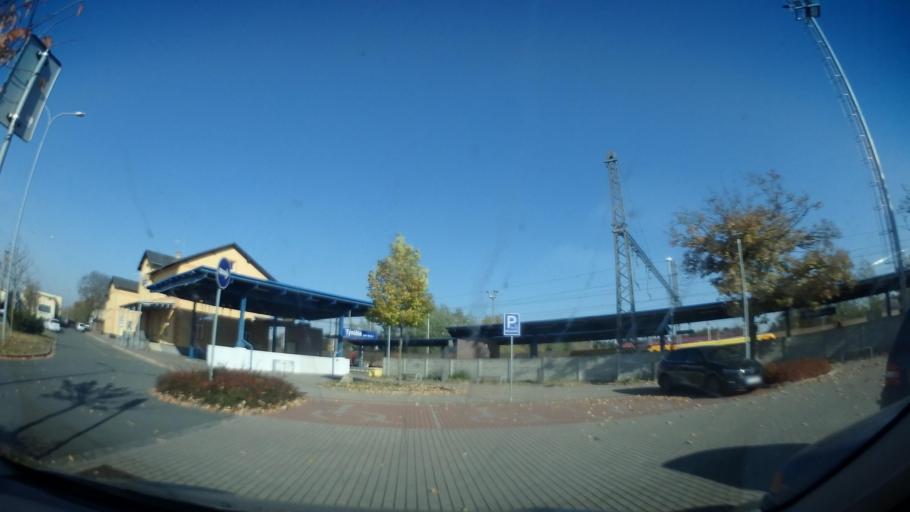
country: CZ
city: Tyniste nad Orlici
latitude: 50.1540
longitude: 16.0743
